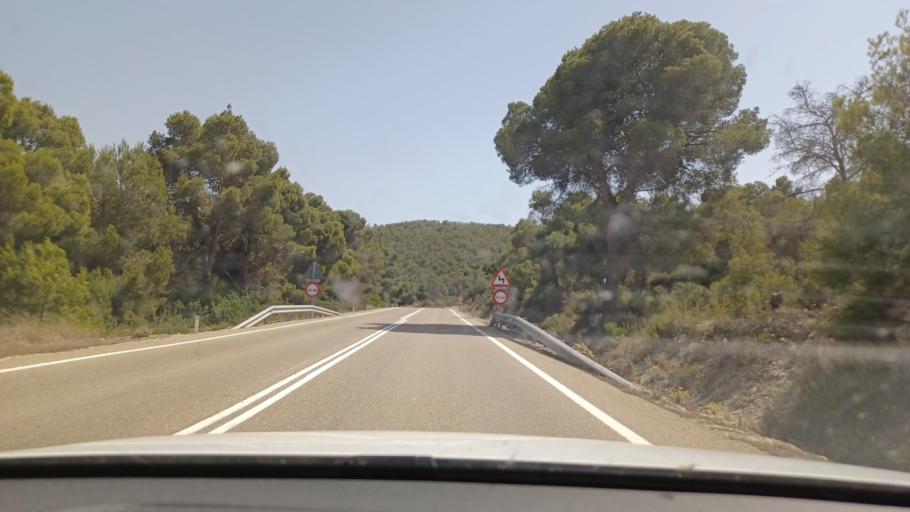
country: ES
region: Aragon
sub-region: Provincia de Zaragoza
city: Chiprana
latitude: 41.3561
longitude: -0.1003
